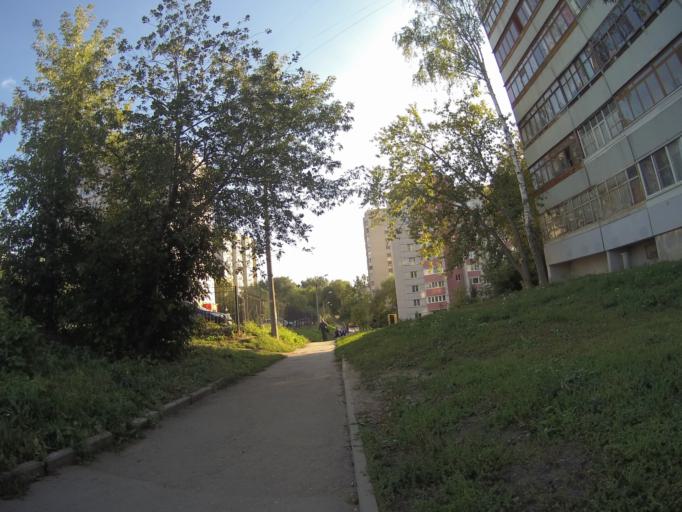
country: RU
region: Vladimir
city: Vladimir
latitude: 56.1494
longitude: 40.3682
